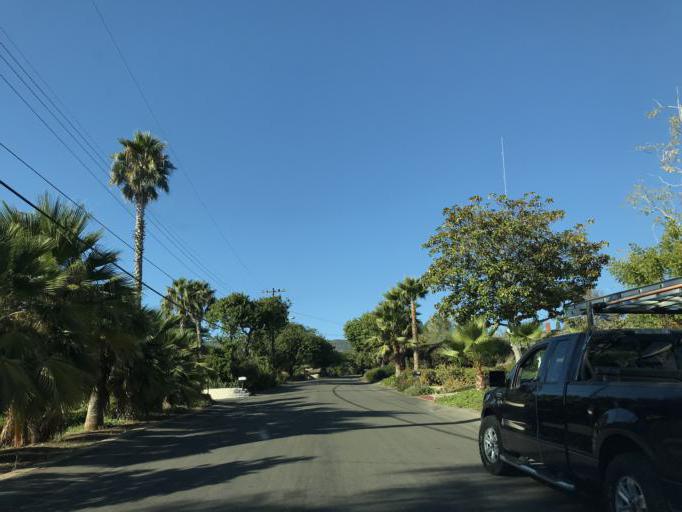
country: US
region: California
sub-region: Santa Barbara County
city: Goleta
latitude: 34.4607
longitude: -119.8211
